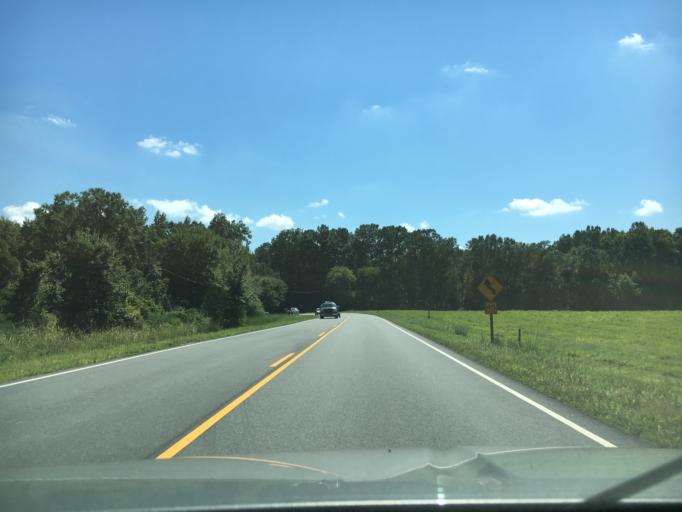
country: US
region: Virginia
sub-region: Amelia County
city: Amelia Court House
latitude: 37.4127
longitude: -77.8939
